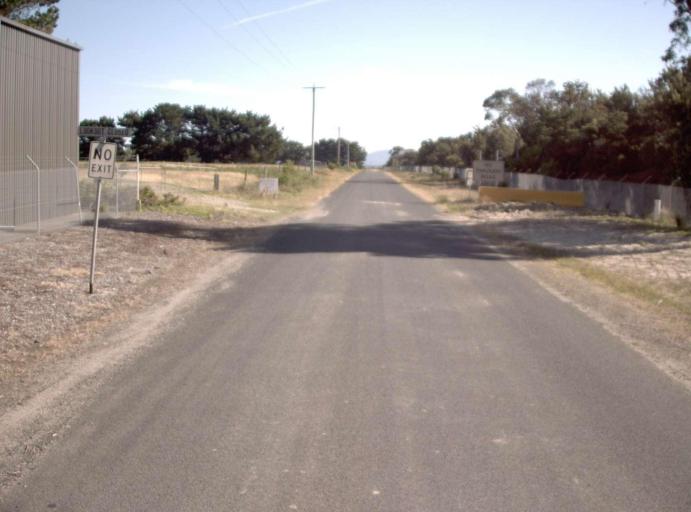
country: AU
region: Victoria
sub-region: Latrobe
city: Morwell
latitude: -38.7113
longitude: 146.3965
